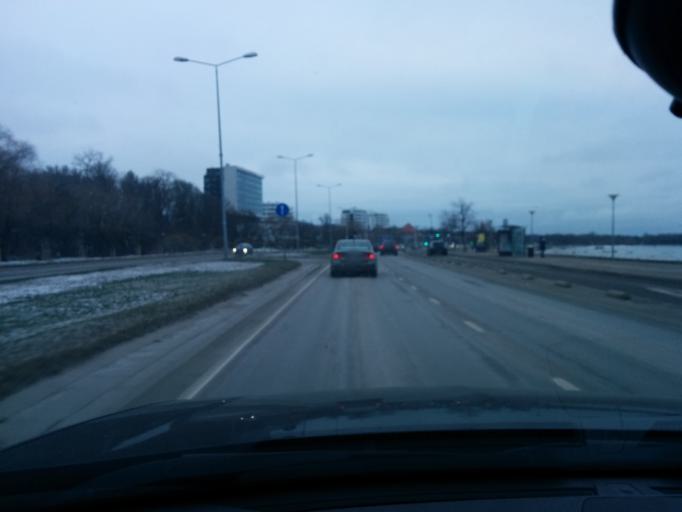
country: EE
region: Harju
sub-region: Tallinna linn
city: Tallinn
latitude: 59.4523
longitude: 24.8074
